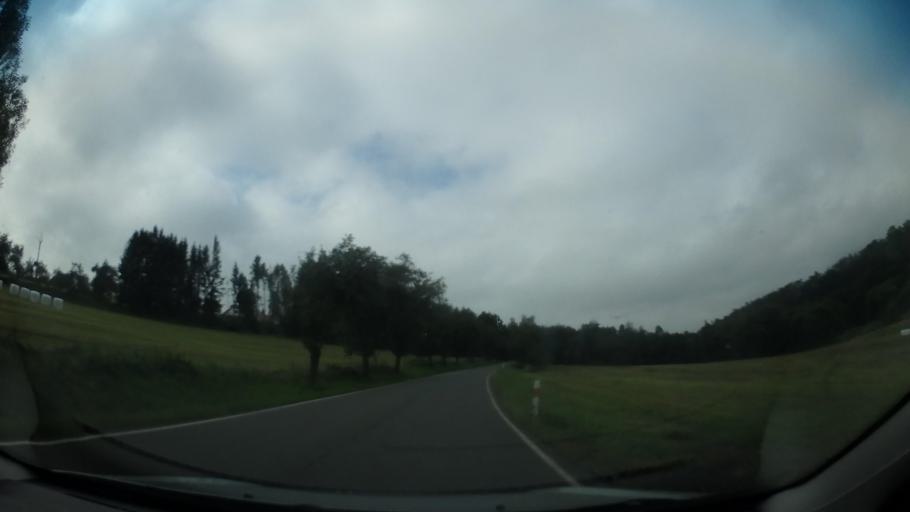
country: CZ
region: Central Bohemia
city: Kosova Hora
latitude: 49.7183
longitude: 14.4647
